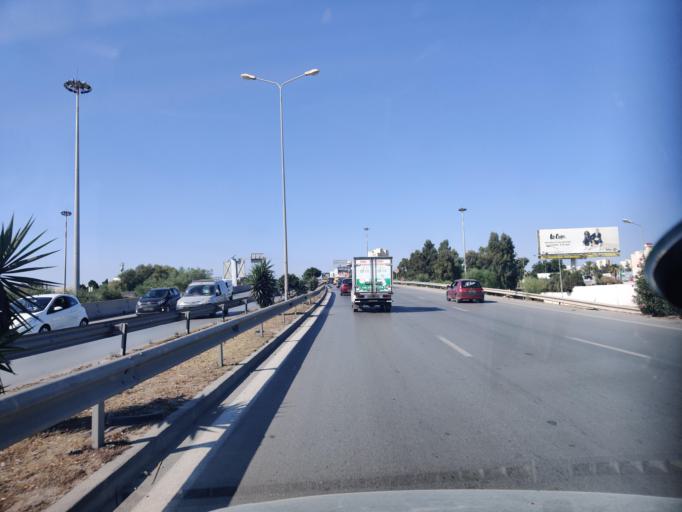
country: TN
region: Ariana
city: Ariana
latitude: 36.8487
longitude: 10.1848
